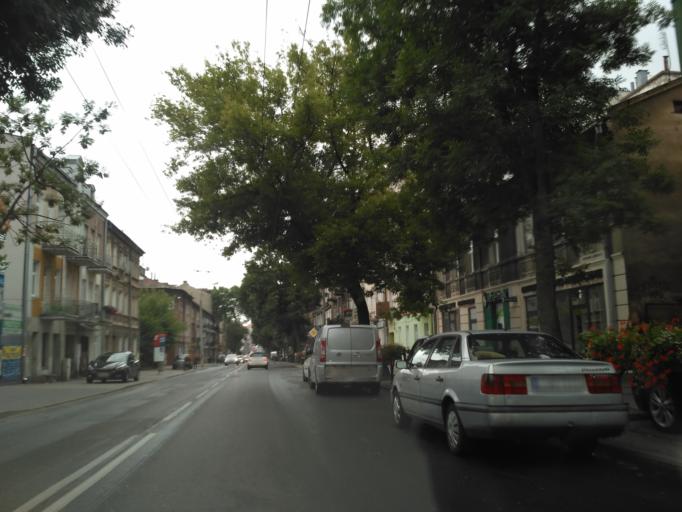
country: PL
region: Lublin Voivodeship
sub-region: Powiat lubelski
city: Lublin
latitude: 51.2558
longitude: 22.5705
